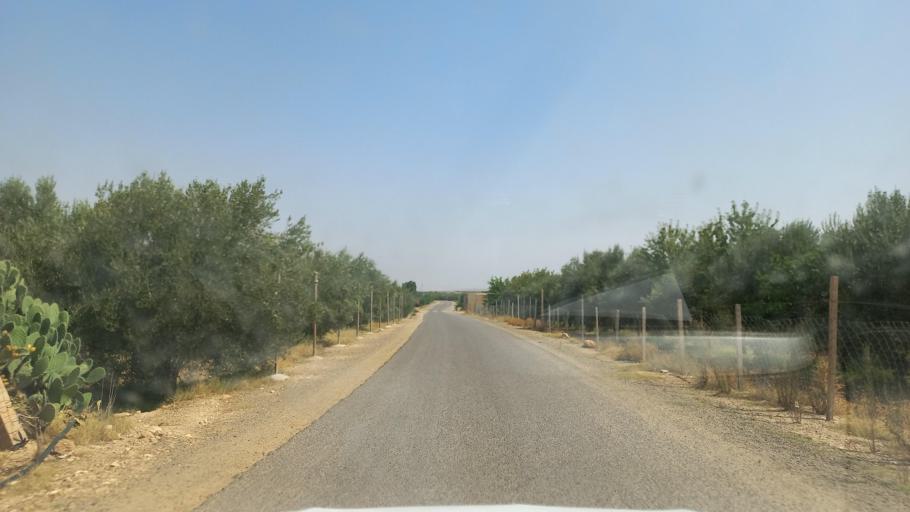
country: TN
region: Al Qasrayn
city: Kasserine
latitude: 35.2382
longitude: 9.0333
